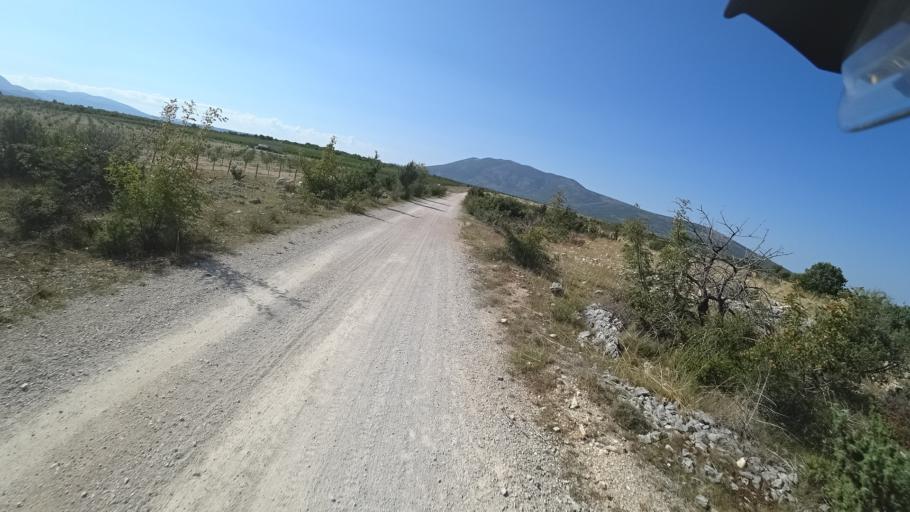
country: HR
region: Sibensko-Kniniska
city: Knin
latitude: 43.9934
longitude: 16.1931
